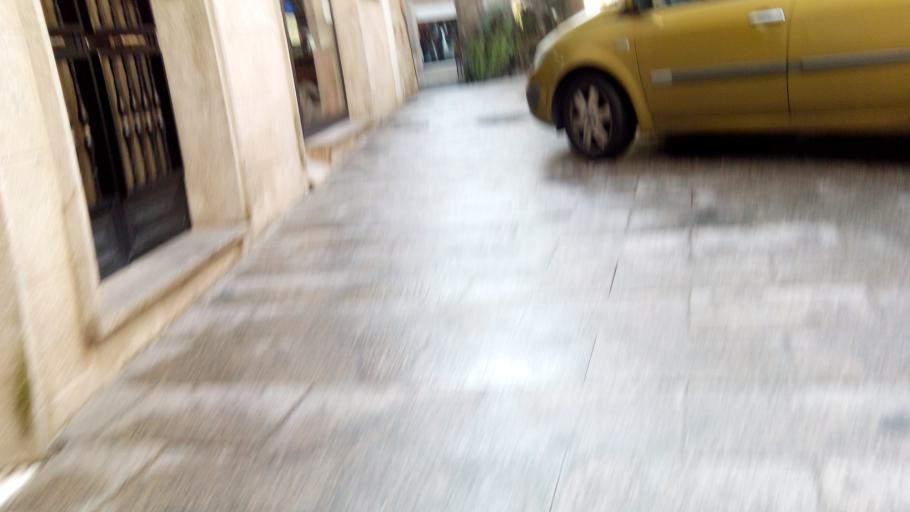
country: ES
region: Galicia
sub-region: Provincia de Pontevedra
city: Marin
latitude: 42.3928
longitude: -8.7033
